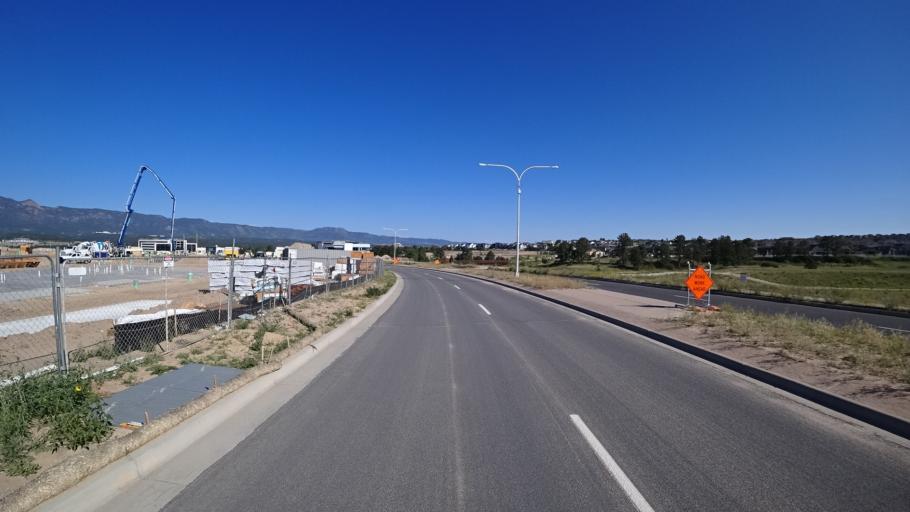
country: US
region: Colorado
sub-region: El Paso County
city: Gleneagle
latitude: 38.9961
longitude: -104.8039
